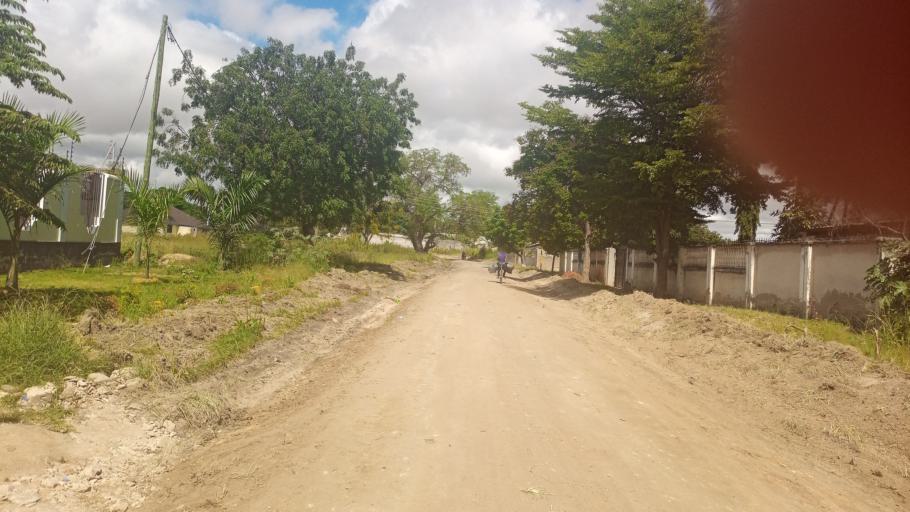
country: TZ
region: Dodoma
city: Dodoma
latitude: -6.1911
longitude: 35.7304
